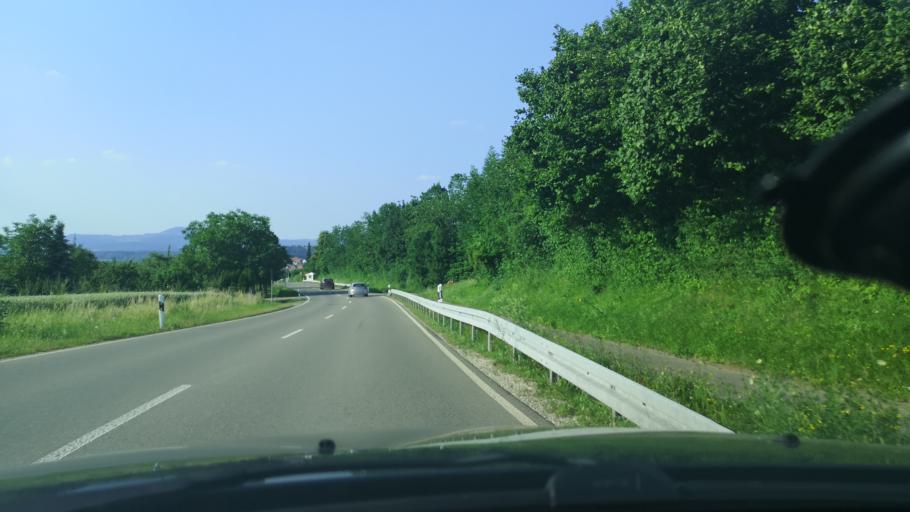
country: DE
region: Baden-Wuerttemberg
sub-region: Regierungsbezirk Stuttgart
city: Schlat
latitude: 48.6440
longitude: 9.7027
